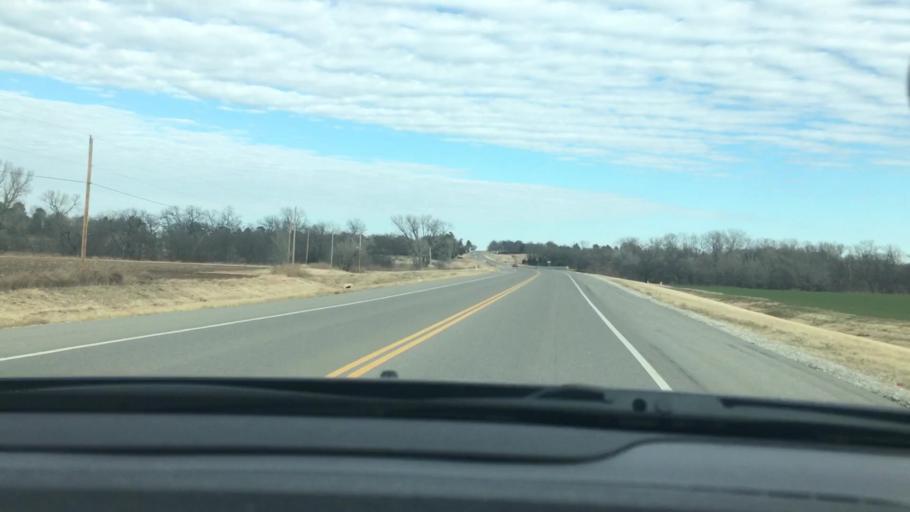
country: US
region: Oklahoma
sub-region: Garvin County
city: Pauls Valley
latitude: 34.7581
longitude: -97.2007
